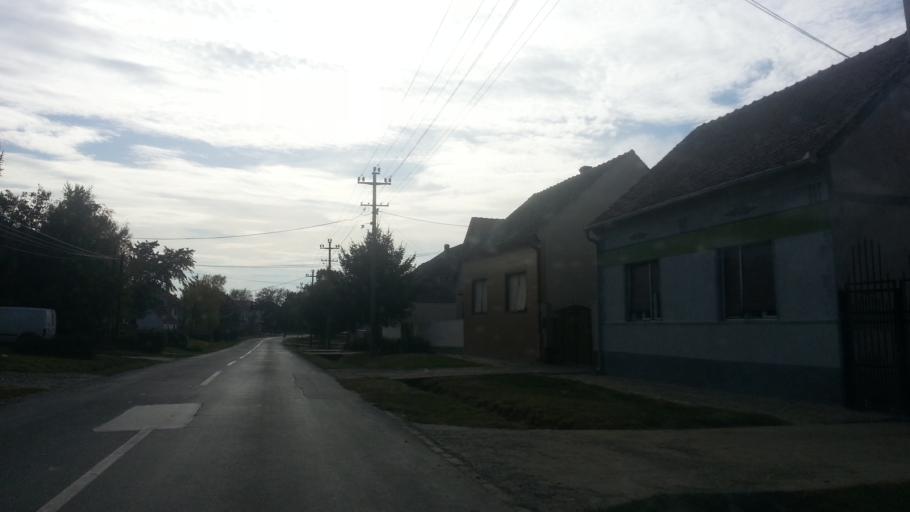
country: RS
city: Belegis
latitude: 45.0117
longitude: 20.3217
